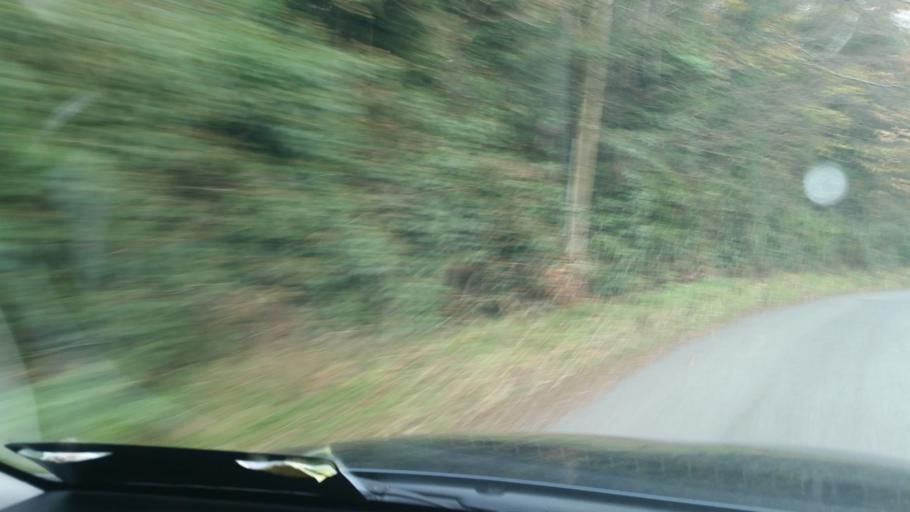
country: IE
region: Leinster
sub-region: An Mhi
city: Duleek
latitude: 53.6958
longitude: -6.4319
